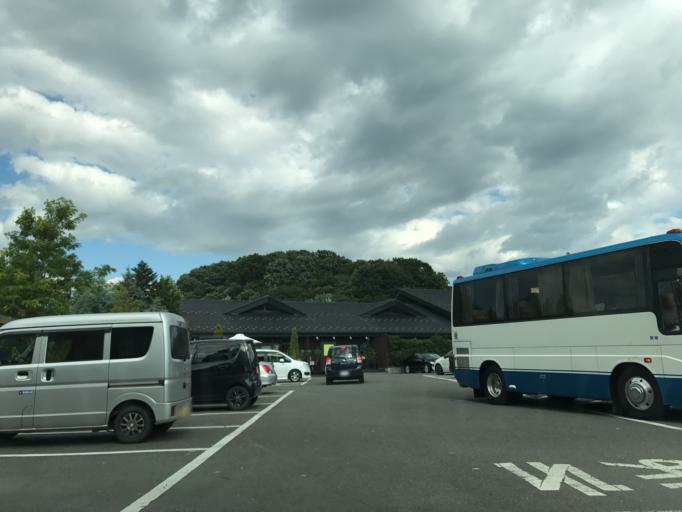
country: JP
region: Fukushima
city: Miharu
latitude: 37.3883
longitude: 140.4504
